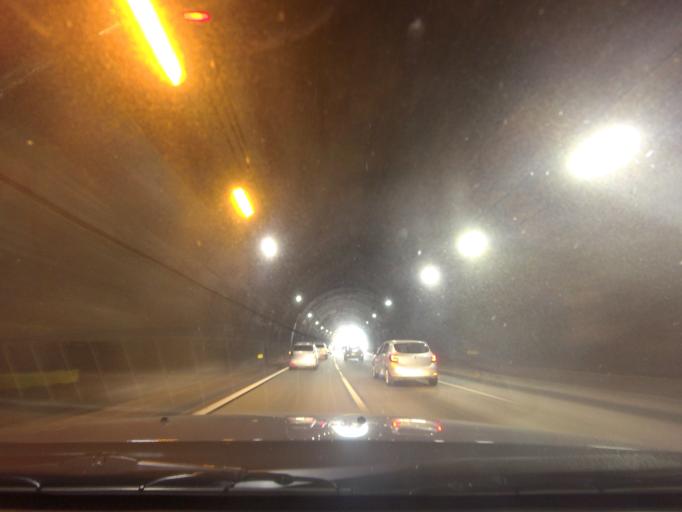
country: BR
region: Sao Paulo
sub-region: Cubatao
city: Cubatao
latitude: -23.9173
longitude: -46.5238
